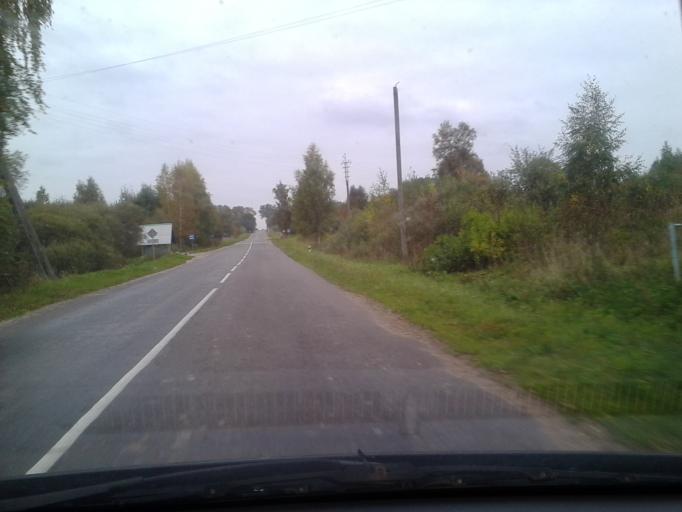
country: BY
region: Vitebsk
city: Pastavy
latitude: 55.1255
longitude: 26.9323
